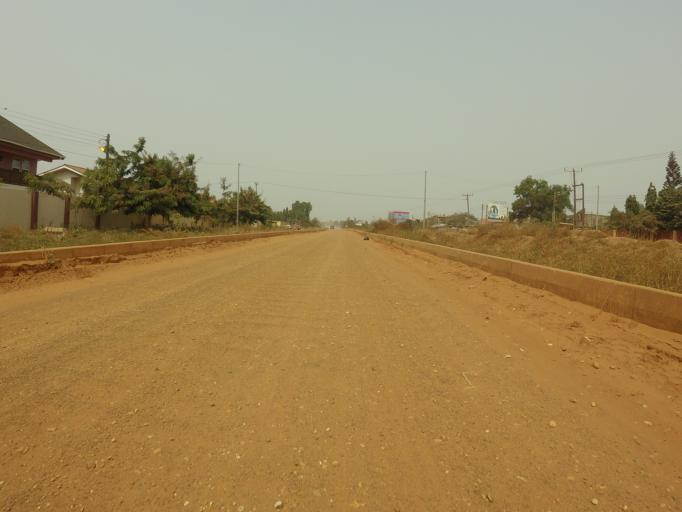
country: GH
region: Greater Accra
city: Teshi Old Town
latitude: 5.6274
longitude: -0.1244
